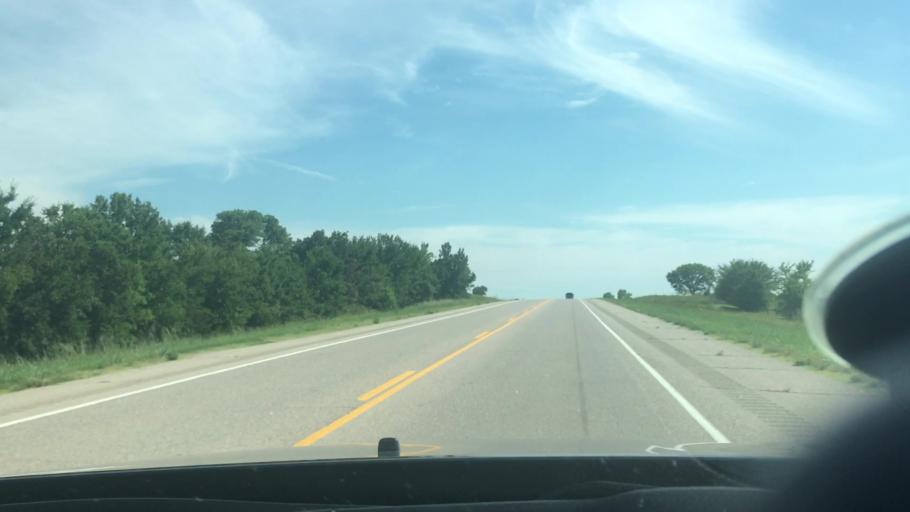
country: US
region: Oklahoma
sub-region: Seminole County
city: Maud
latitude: 35.0930
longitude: -96.6789
